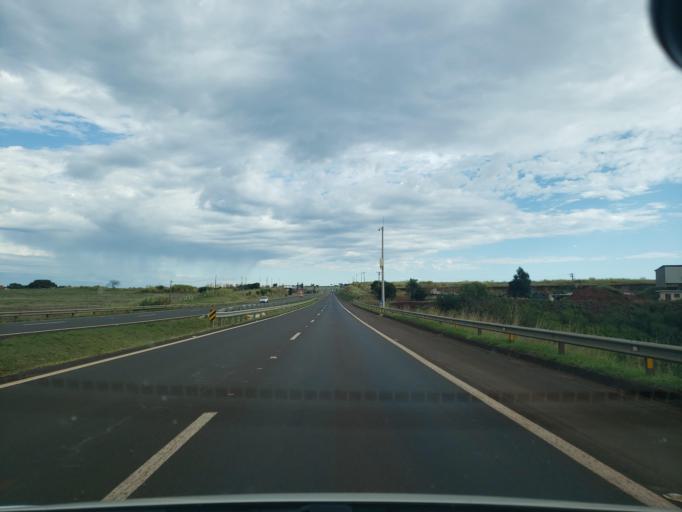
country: BR
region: Sao Paulo
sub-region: Jau
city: Jau
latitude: -22.2620
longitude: -48.5327
